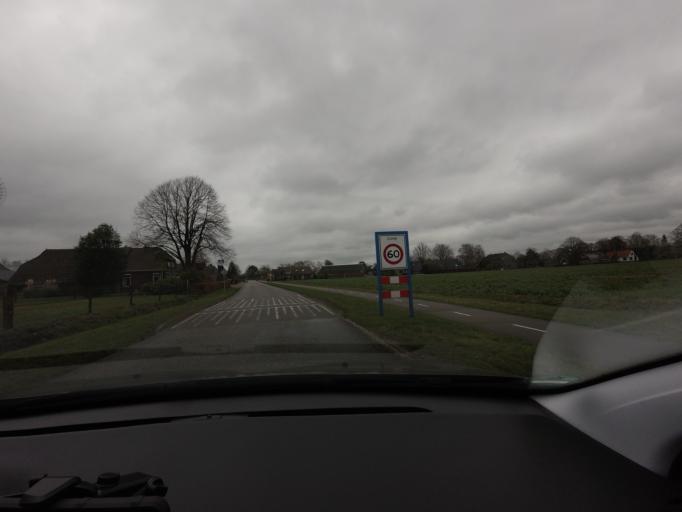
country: NL
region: Drenthe
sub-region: Gemeente Hoogeveen
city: Hoogeveen
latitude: 52.8425
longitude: 6.5344
